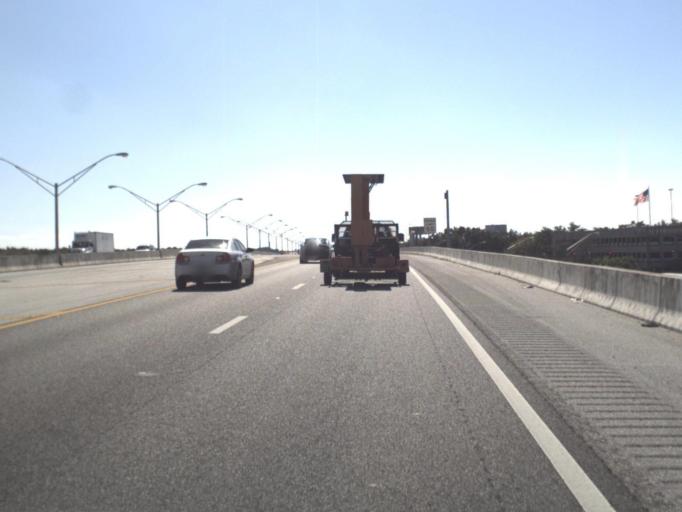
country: US
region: Florida
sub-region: Hillsborough County
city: Town 'n' Country
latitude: 27.9829
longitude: -82.5466
